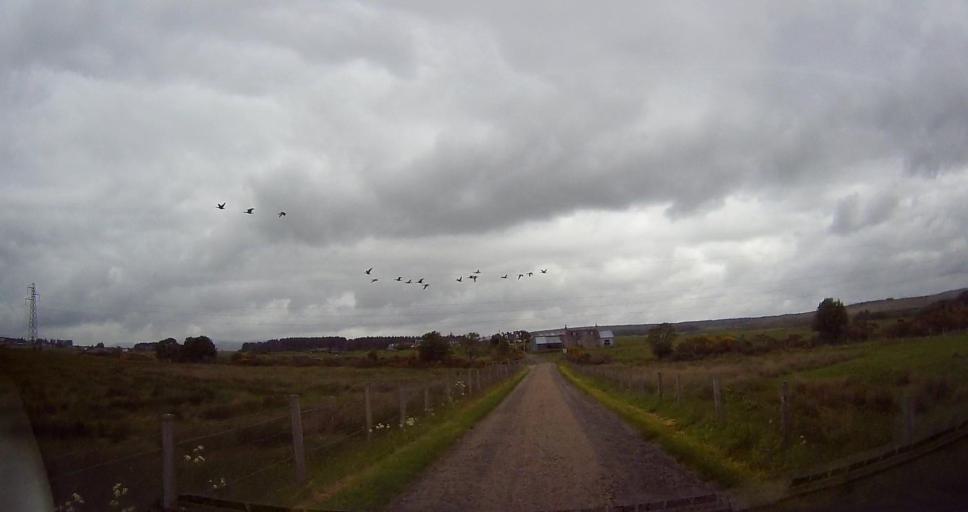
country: GB
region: Scotland
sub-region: Highland
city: Alness
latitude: 58.0599
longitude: -4.4306
